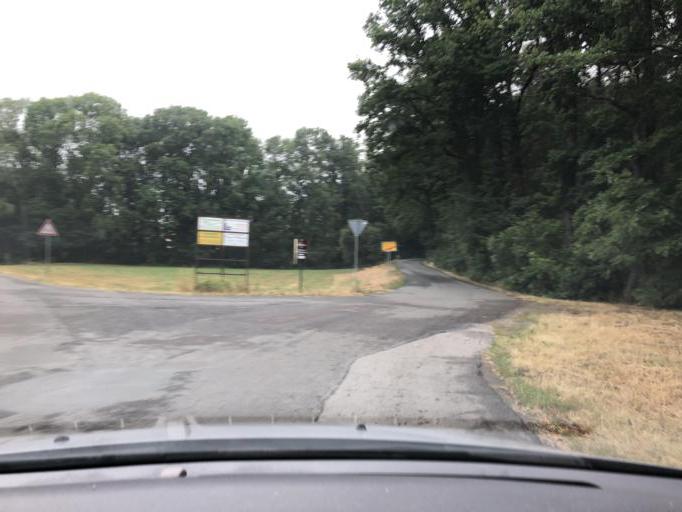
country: DE
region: Thuringia
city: Langenleuba-Niederhain
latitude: 51.0011
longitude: 12.6166
